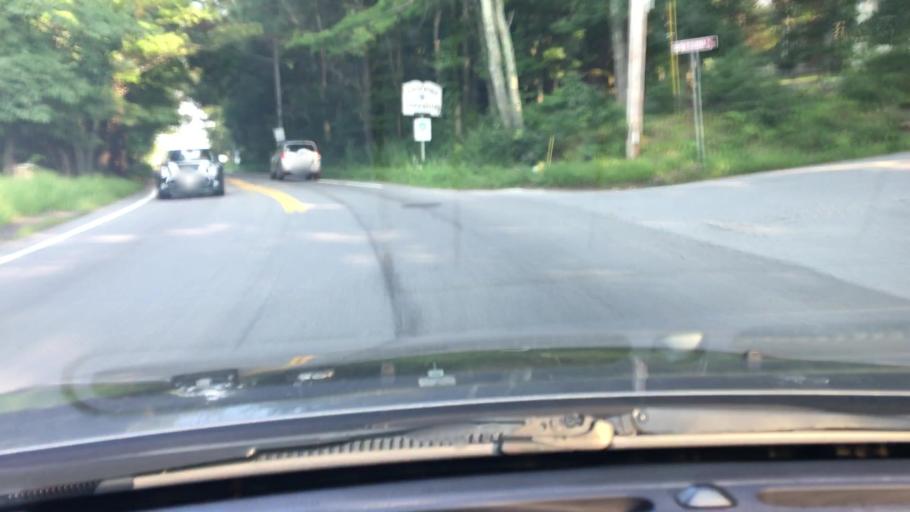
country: US
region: Massachusetts
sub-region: Worcester County
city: Westborough
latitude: 42.2513
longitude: -71.5902
